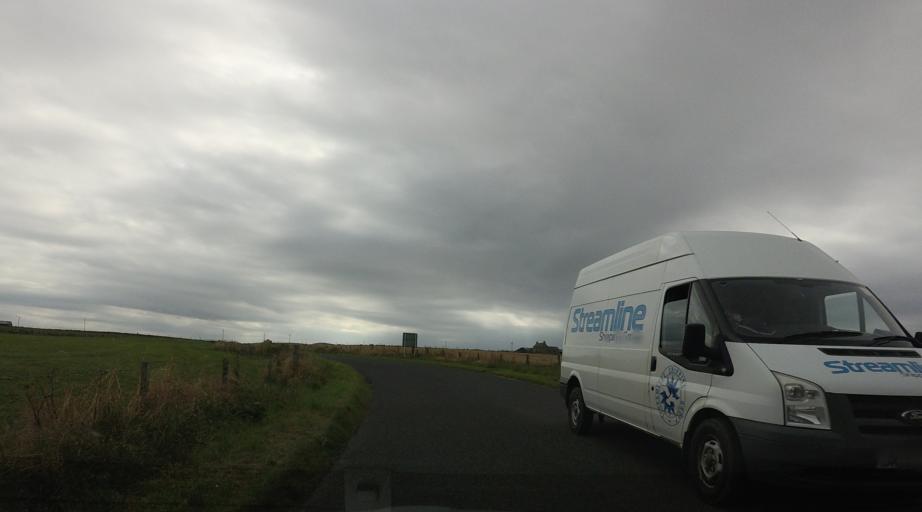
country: GB
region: Scotland
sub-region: Orkney Islands
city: Stromness
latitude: 59.0396
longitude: -3.3109
